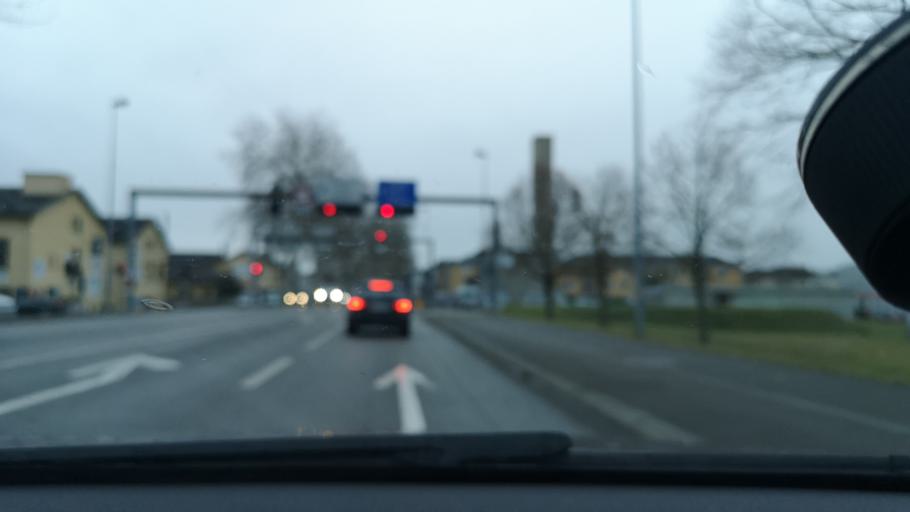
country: CH
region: Vaud
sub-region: Jura-Nord vaudois District
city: Yverdon-les-Bains
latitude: 46.7890
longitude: 6.6300
